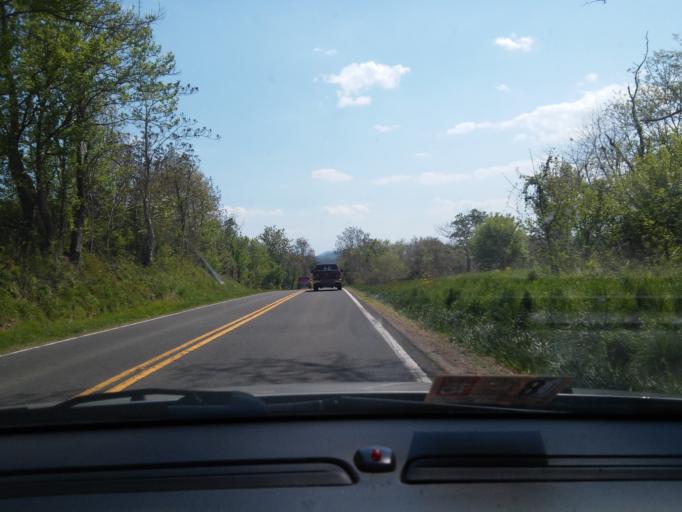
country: US
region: Virginia
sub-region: Rappahannock County
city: Washington
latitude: 38.7366
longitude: -78.1106
